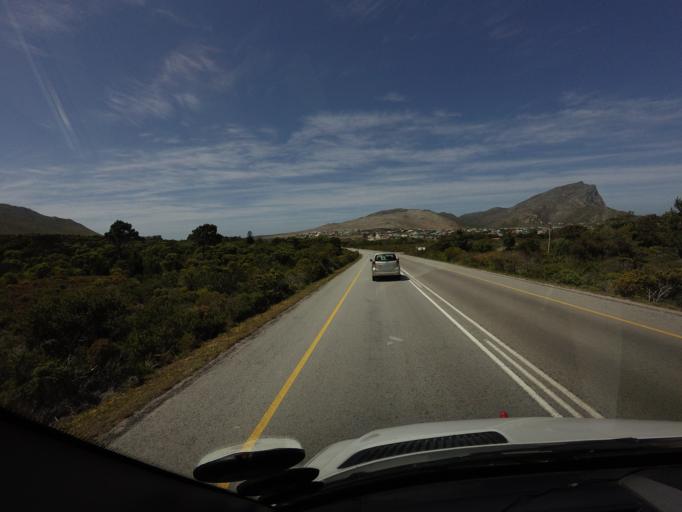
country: ZA
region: Western Cape
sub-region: Overberg District Municipality
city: Grabouw
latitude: -34.3376
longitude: 18.8419
